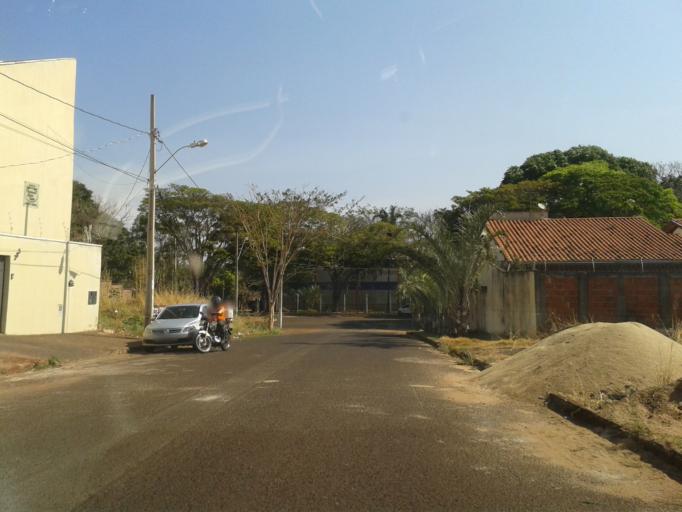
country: BR
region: Minas Gerais
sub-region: Ituiutaba
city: Ituiutaba
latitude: -18.9717
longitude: -49.4459
